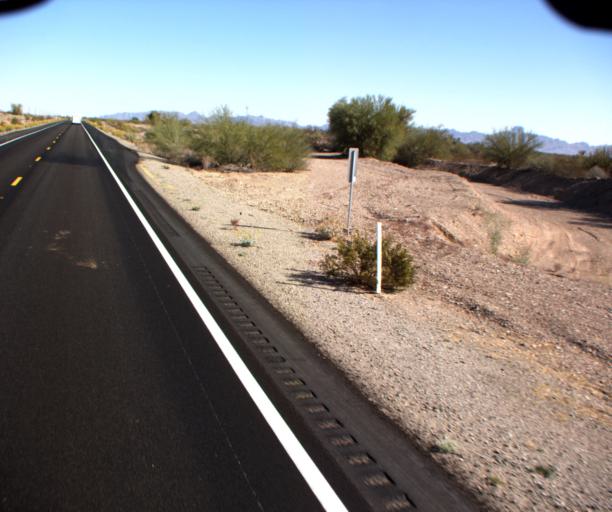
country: US
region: Arizona
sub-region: Yuma County
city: Wellton
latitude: 32.9713
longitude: -114.2907
